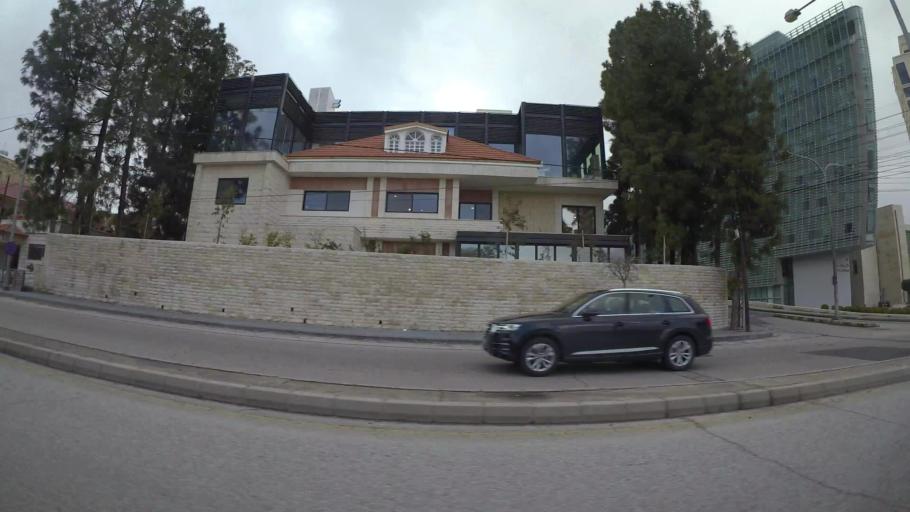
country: JO
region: Amman
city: Wadi as Sir
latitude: 31.9563
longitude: 35.8782
